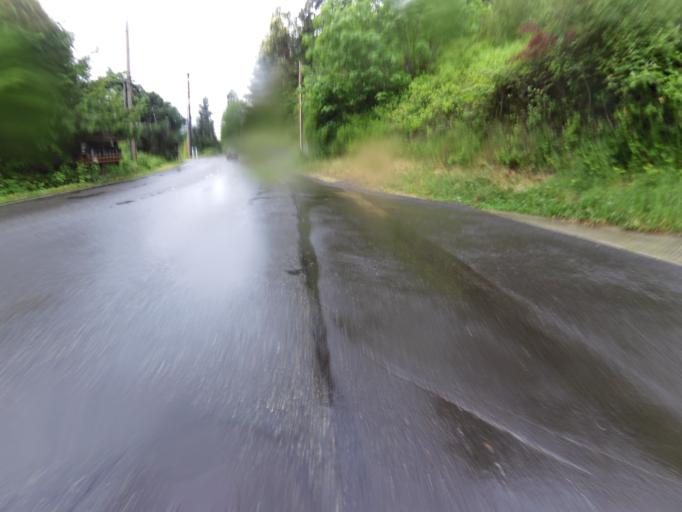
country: US
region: Washington
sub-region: King County
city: Bryn Mawr-Skyway
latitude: 47.5306
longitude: -122.2360
